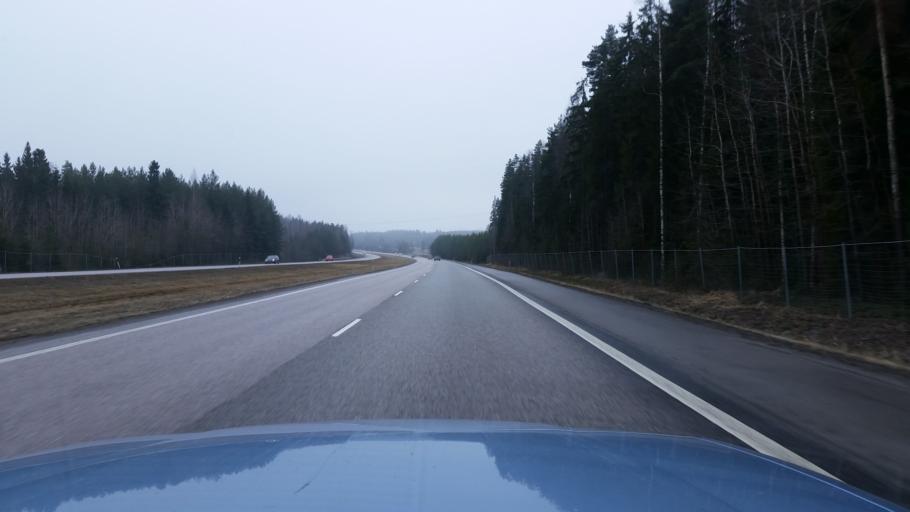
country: FI
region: Uusimaa
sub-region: Helsinki
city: Nurmijaervi
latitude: 60.4315
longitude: 24.8288
